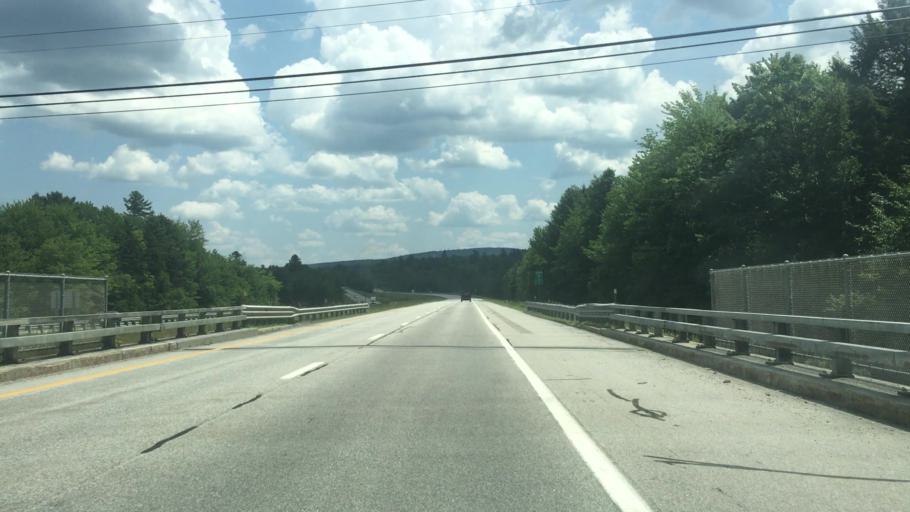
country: US
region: New Hampshire
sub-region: Merrimack County
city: New London
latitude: 43.4092
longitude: -72.0261
